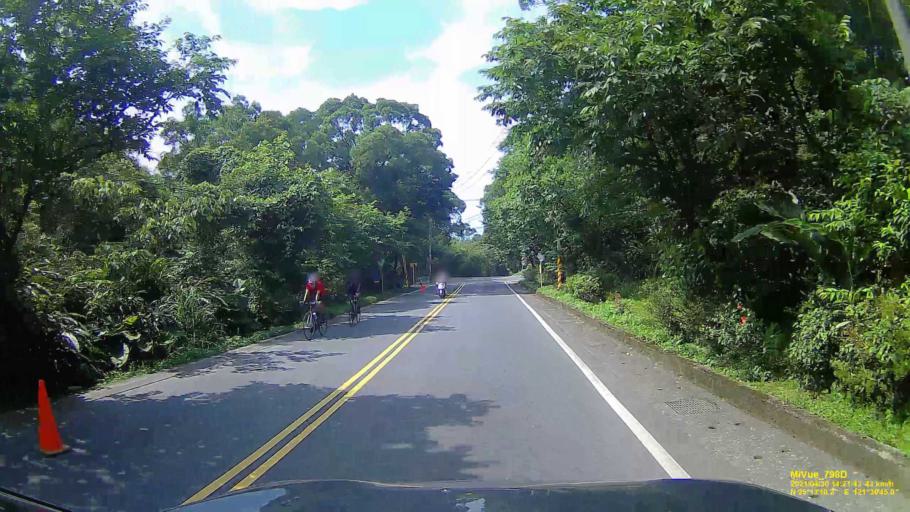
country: TW
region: Taipei
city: Taipei
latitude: 25.2197
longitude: 121.5125
